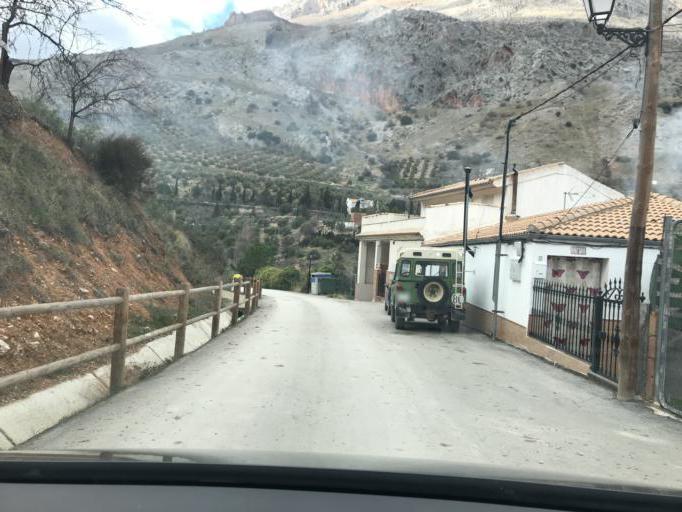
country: ES
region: Andalusia
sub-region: Provincia de Jaen
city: Torres
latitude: 37.7947
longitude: -3.4653
